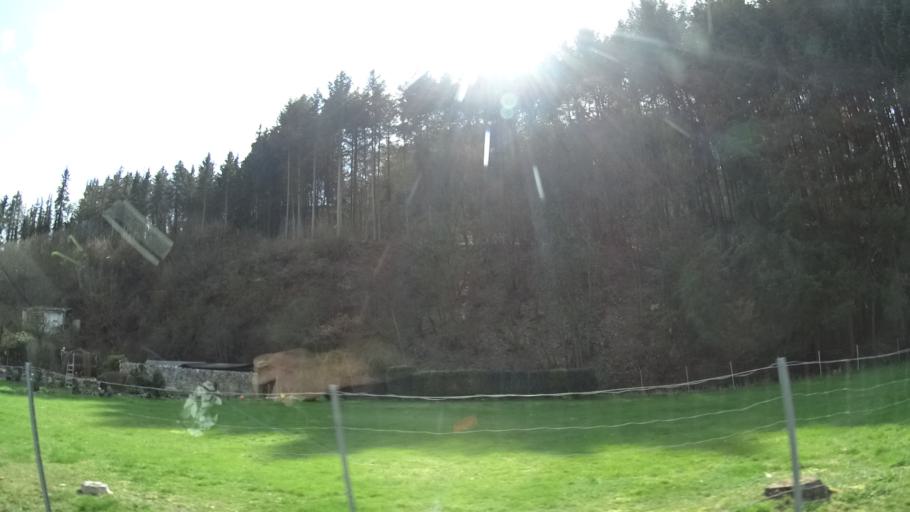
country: DE
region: Rheinland-Pfalz
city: Barenbach
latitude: 49.7506
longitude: 7.4369
